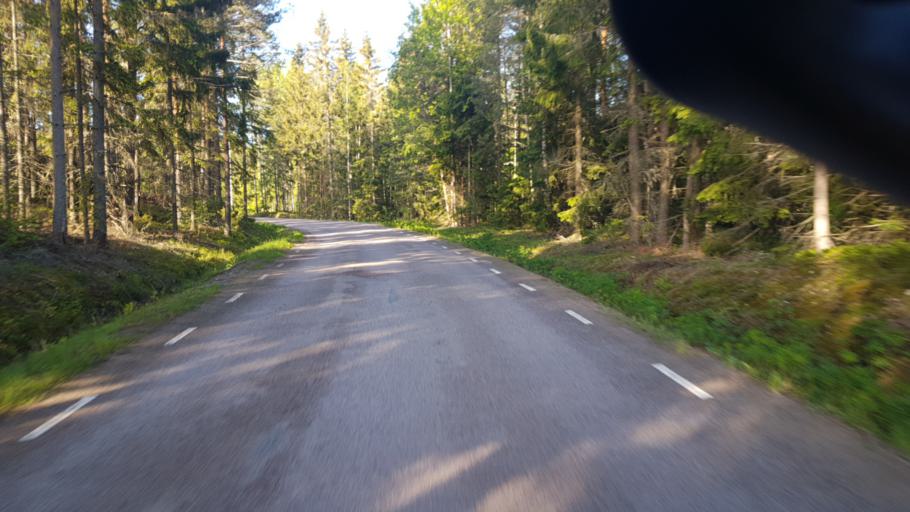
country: SE
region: Vaermland
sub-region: Arvika Kommun
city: Arvika
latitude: 59.5461
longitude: 12.5202
